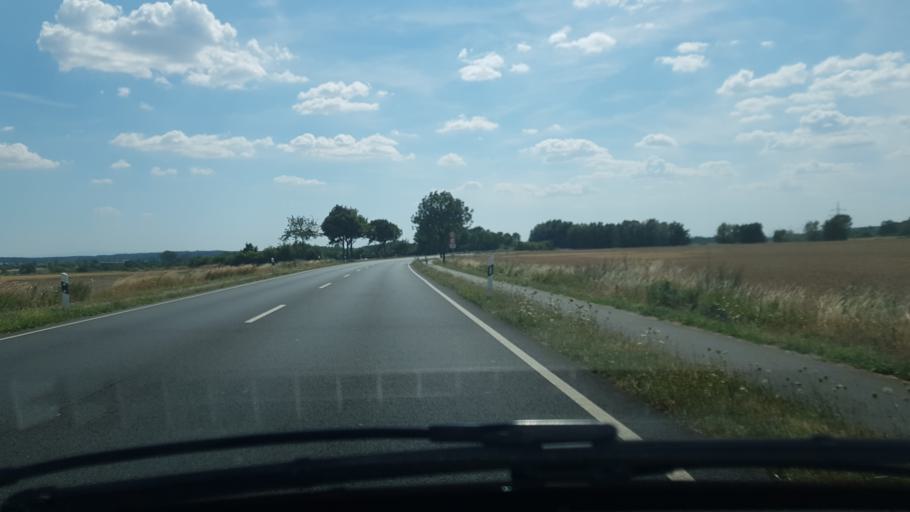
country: DE
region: Lower Saxony
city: Lehre
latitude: 52.3468
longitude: 10.6884
